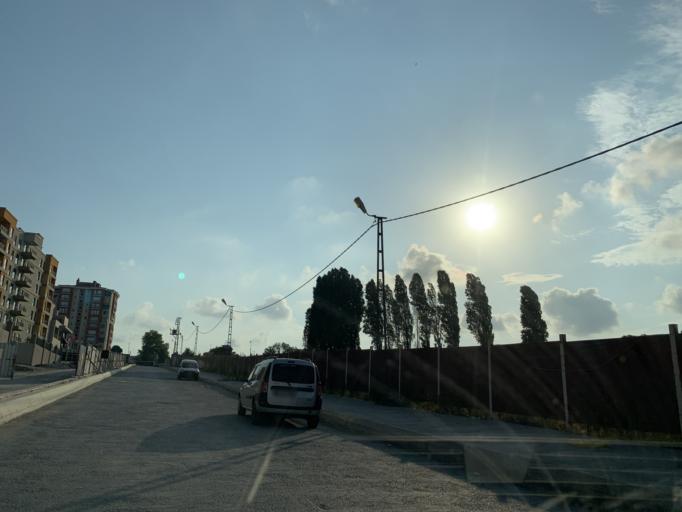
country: TR
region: Istanbul
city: Esenyurt
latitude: 41.0476
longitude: 28.6767
